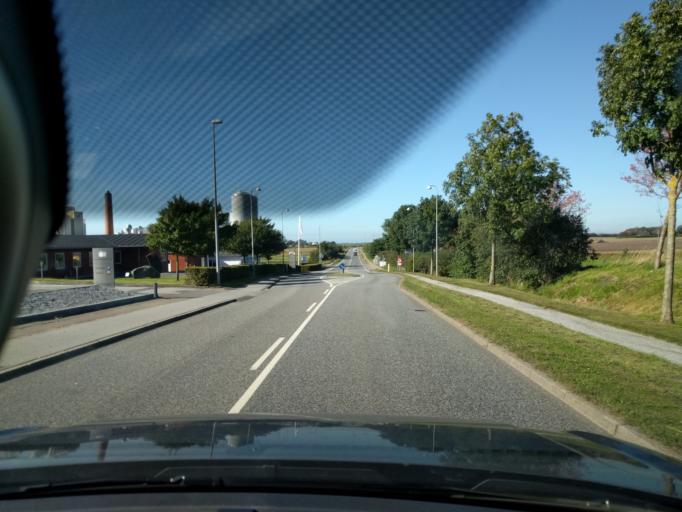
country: DK
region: North Denmark
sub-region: Vesthimmerland Kommune
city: Alestrup
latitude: 56.7102
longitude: 9.6234
